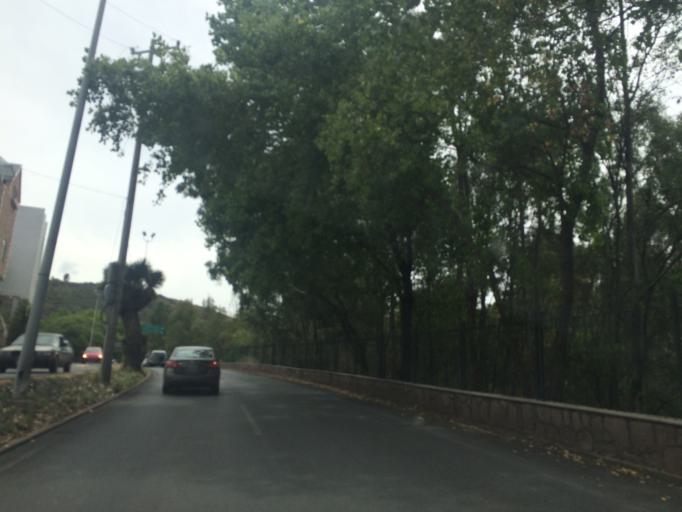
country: MX
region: Zacatecas
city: Zacatecas
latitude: 22.7613
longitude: -102.5569
